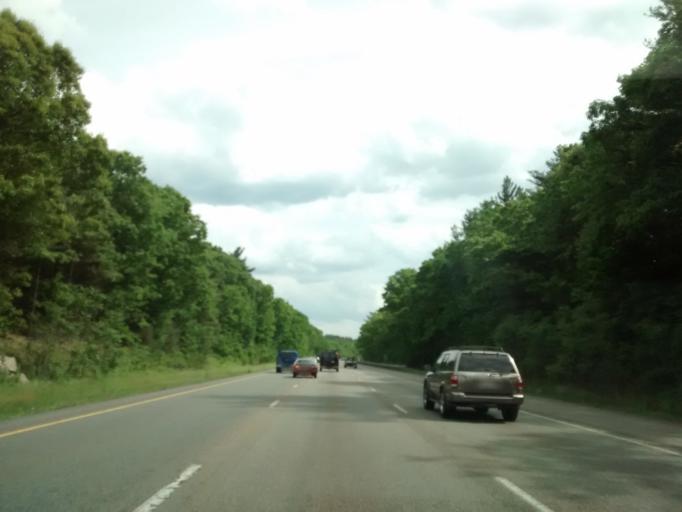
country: US
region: Massachusetts
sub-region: Worcester County
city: Cordaville
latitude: 42.2521
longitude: -71.5587
